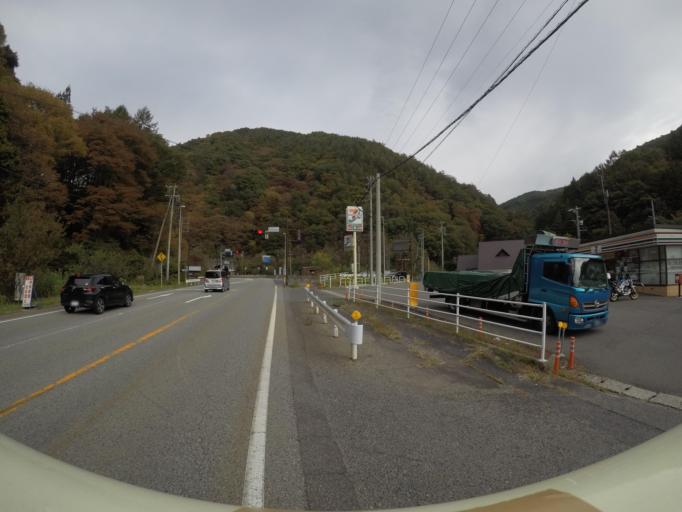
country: JP
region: Nagano
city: Ina
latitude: 35.9023
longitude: 137.7740
